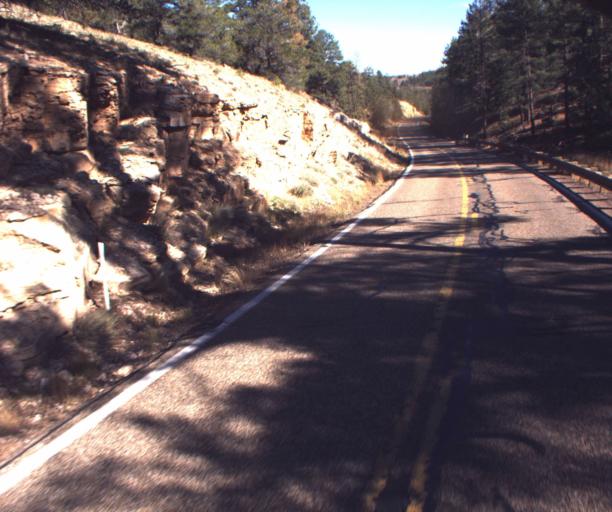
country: US
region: Arizona
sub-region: Coconino County
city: Fredonia
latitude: 36.7322
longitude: -112.1614
